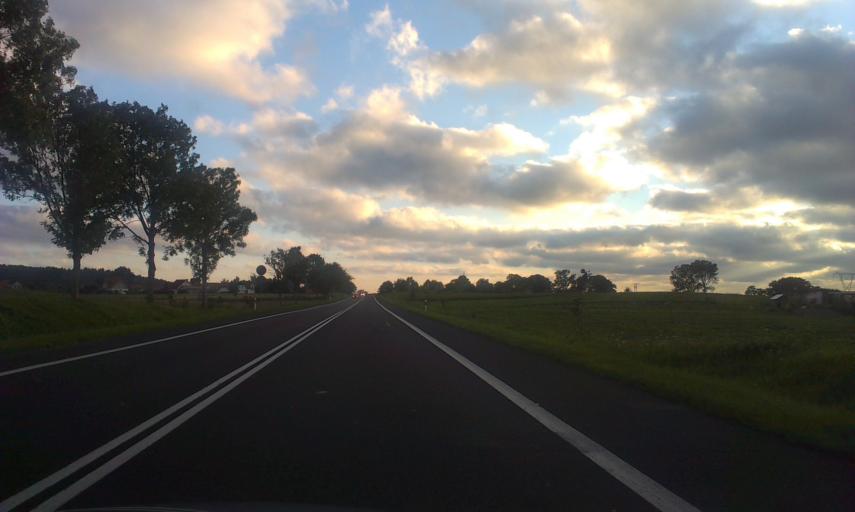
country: PL
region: West Pomeranian Voivodeship
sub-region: Powiat slawienski
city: Darlowo
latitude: 54.2764
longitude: 16.4352
